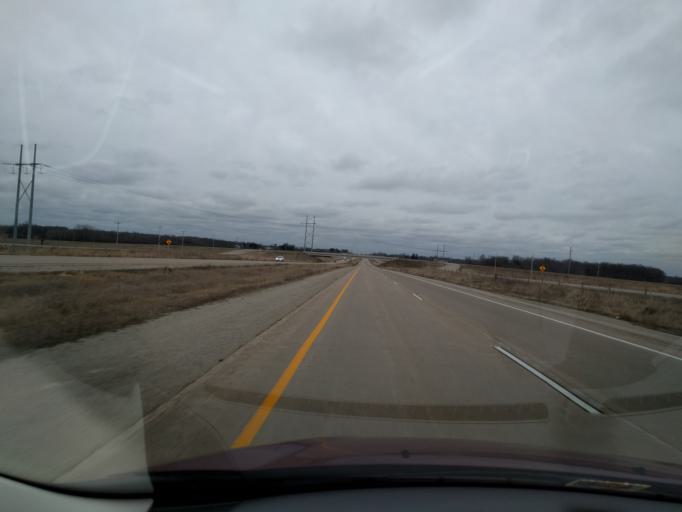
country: US
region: Wisconsin
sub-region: Winnebago County
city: Winneconne
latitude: 44.1734
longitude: -88.6645
